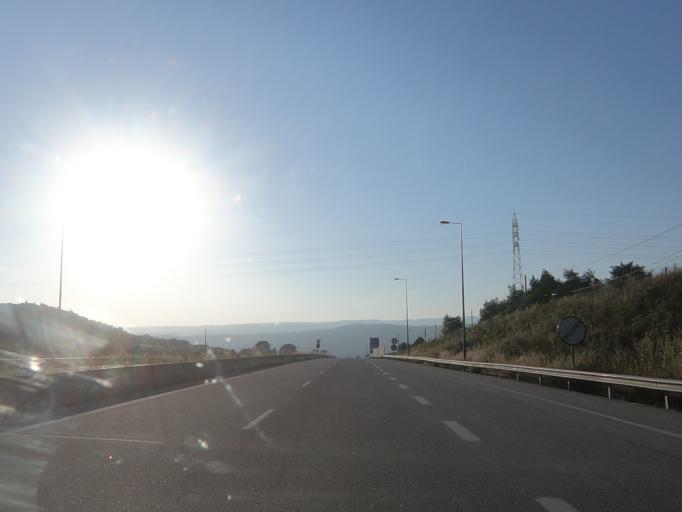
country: PT
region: Guarda
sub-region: Celorico da Beira
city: Celorico da Beira
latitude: 40.6256
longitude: -7.4025
